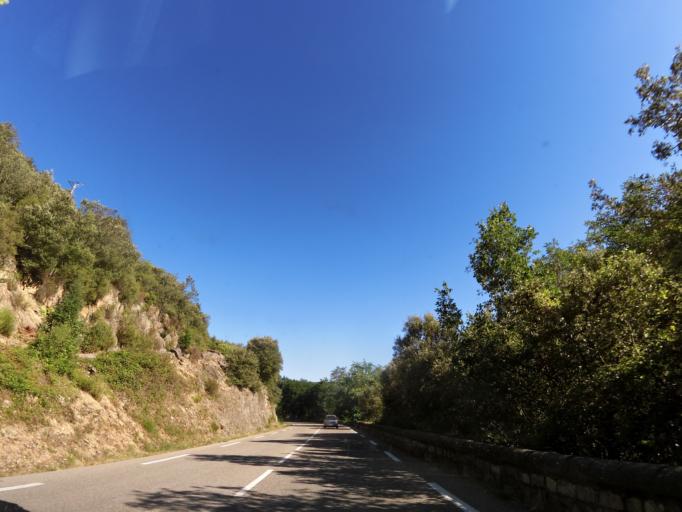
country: FR
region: Languedoc-Roussillon
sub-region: Departement du Gard
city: Valleraugue
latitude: 44.0644
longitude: 3.6812
